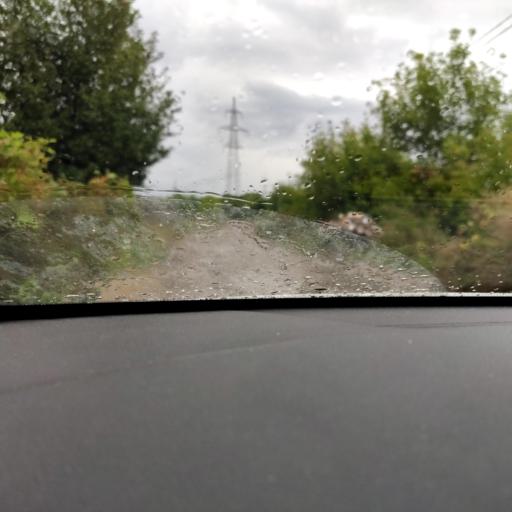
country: RU
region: Tatarstan
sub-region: Gorod Kazan'
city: Kazan
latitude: 55.8327
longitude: 49.2018
